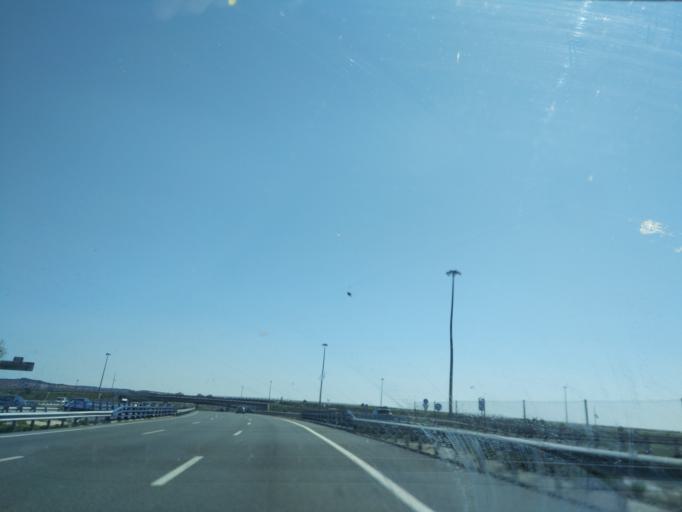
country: ES
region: Madrid
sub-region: Provincia de Madrid
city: Villa de Vallecas
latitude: 40.3606
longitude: -3.5679
